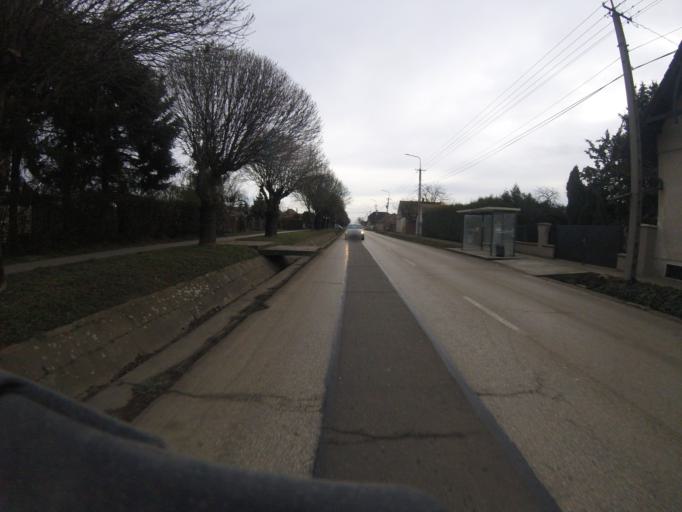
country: HU
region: Tolna
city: Dombovar
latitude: 46.3858
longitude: 18.1539
